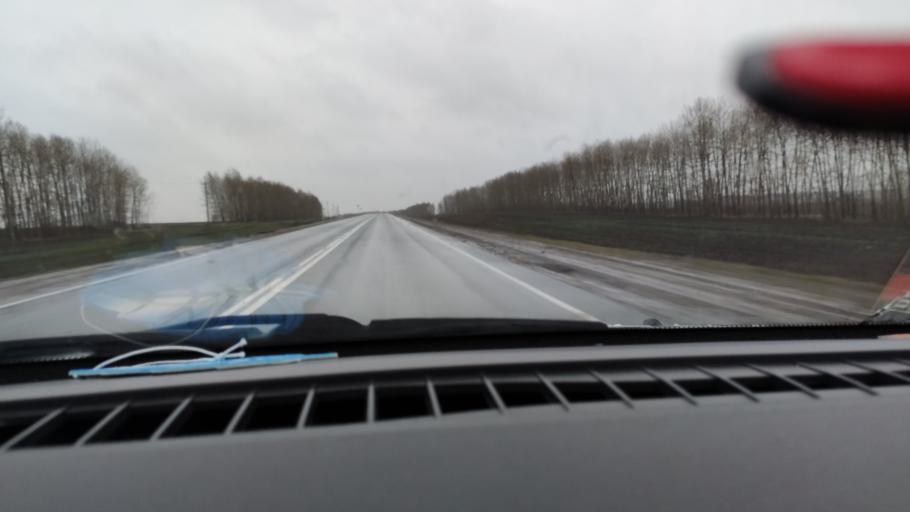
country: RU
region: Tatarstan
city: Mendeleyevsk
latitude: 55.9272
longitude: 52.2787
